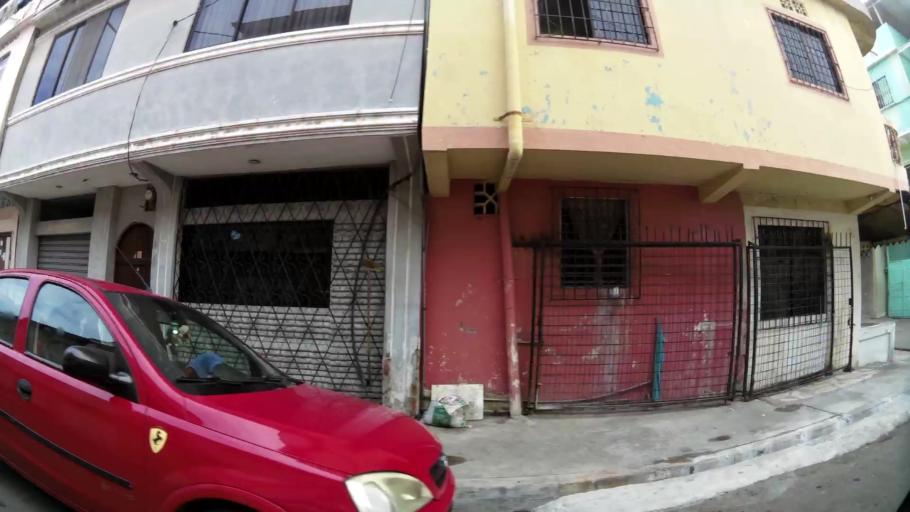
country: EC
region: Guayas
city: Guayaquil
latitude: -2.2441
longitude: -79.8912
